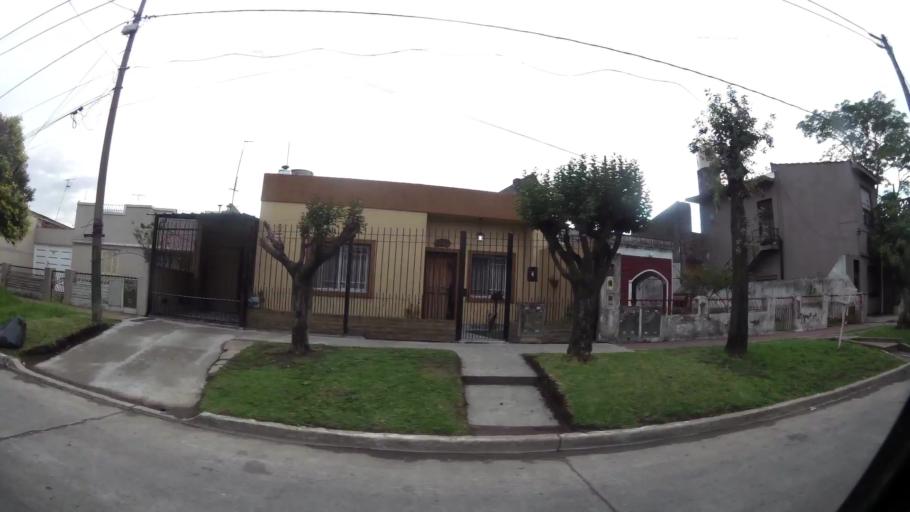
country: AR
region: Buenos Aires
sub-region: Partido de Lomas de Zamora
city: Lomas de Zamora
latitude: -34.7448
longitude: -58.3470
